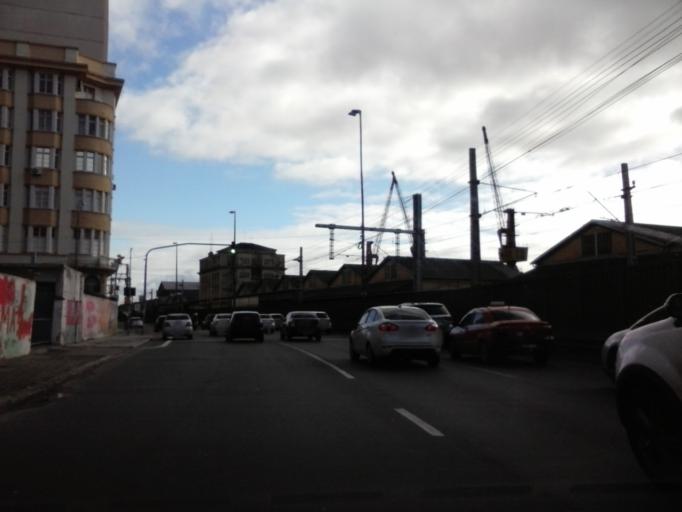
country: BR
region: Rio Grande do Sul
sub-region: Porto Alegre
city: Porto Alegre
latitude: -30.0268
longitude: -51.2289
